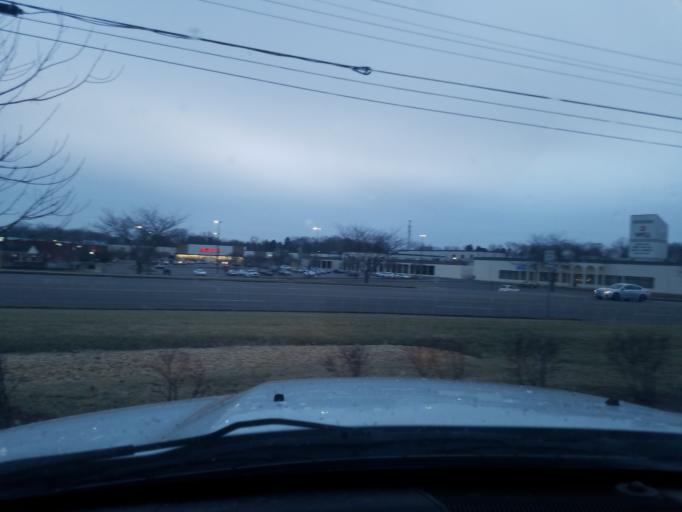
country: US
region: Kentucky
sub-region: Warren County
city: Bowling Green
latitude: 36.9630
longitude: -86.4691
